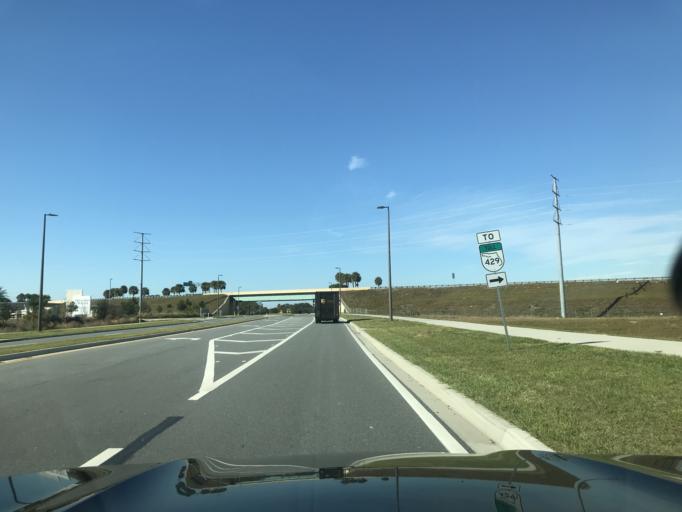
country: US
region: Florida
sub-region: Orange County
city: Oakland
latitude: 28.4599
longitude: -81.6333
